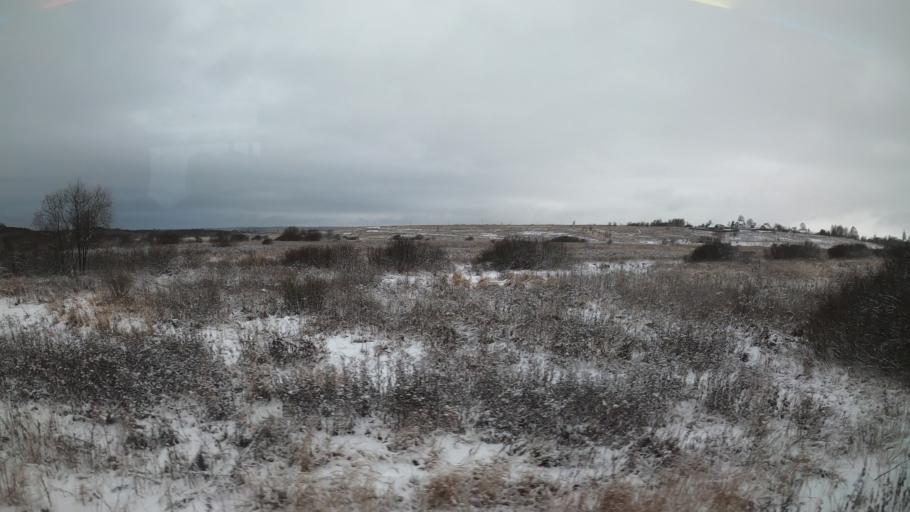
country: RU
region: Jaroslavl
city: Pereslavl'-Zalesskiy
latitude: 56.6970
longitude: 38.9171
